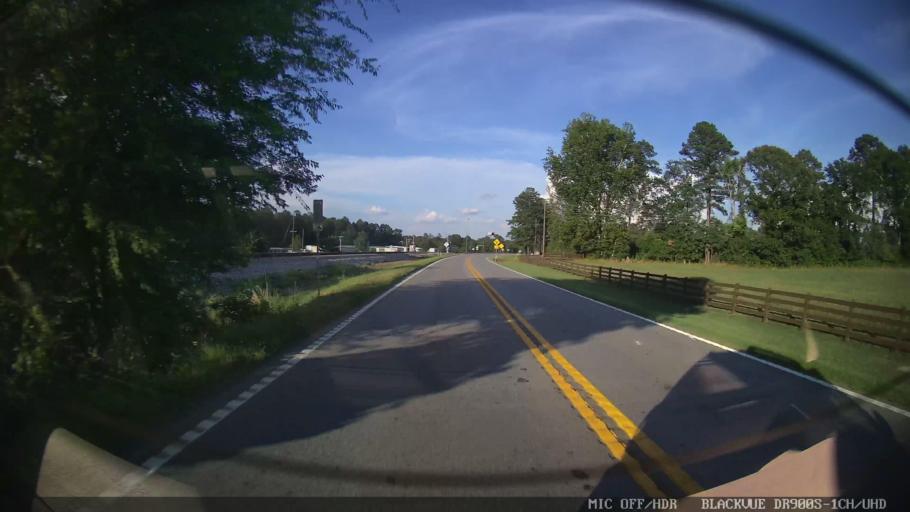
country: US
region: Georgia
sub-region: Monroe County
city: Forsyth
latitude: 32.9507
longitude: -83.8298
